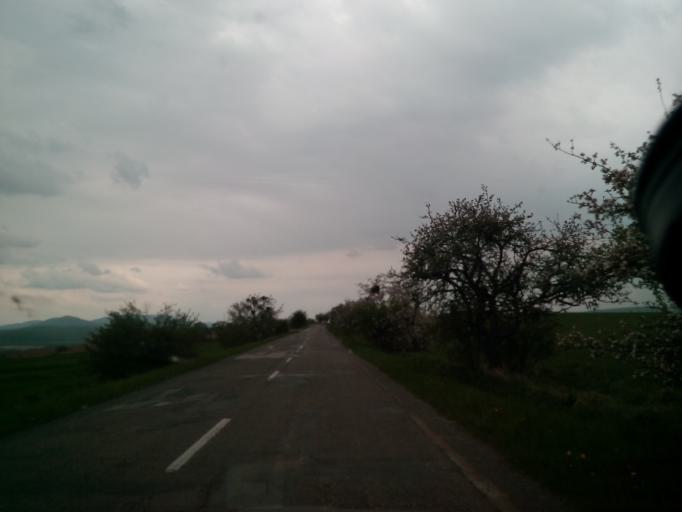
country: SK
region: Kosicky
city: Secovce
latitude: 48.7674
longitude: 21.4694
